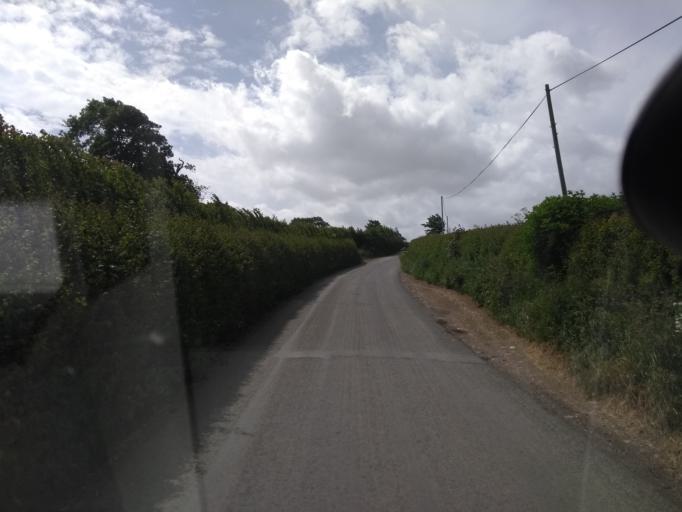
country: GB
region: England
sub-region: Somerset
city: Bridgwater
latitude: 51.1819
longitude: -3.0778
